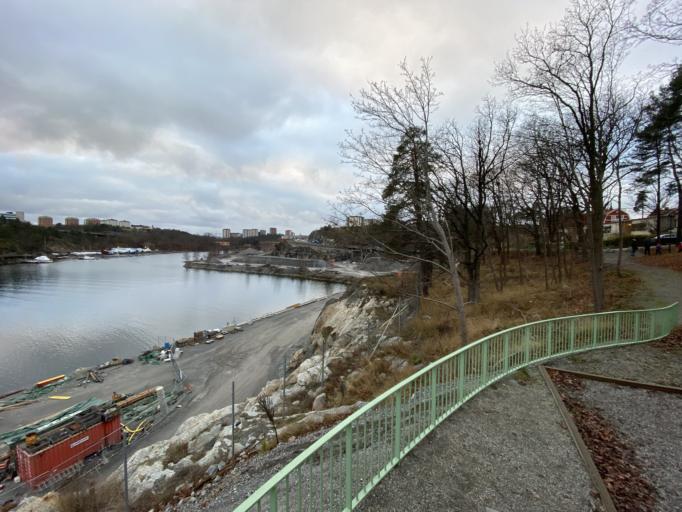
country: SE
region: Stockholm
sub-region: Nacka Kommun
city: Nacka
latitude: 59.3151
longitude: 18.1384
